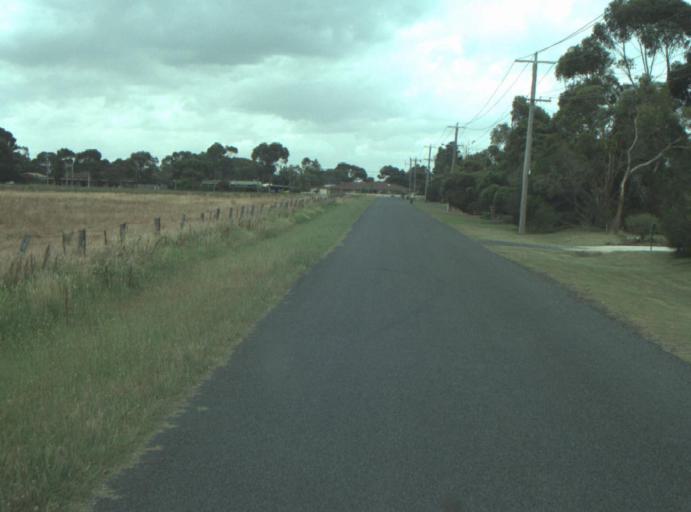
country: AU
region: Victoria
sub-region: Greater Geelong
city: East Geelong
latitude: -38.1748
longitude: 144.4139
